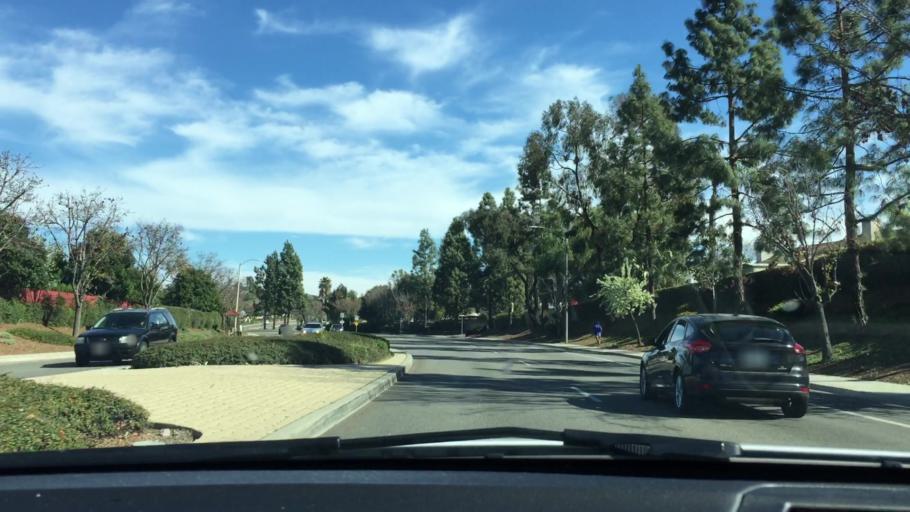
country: US
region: California
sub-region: San Diego County
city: Vista
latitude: 33.2399
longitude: -117.2722
